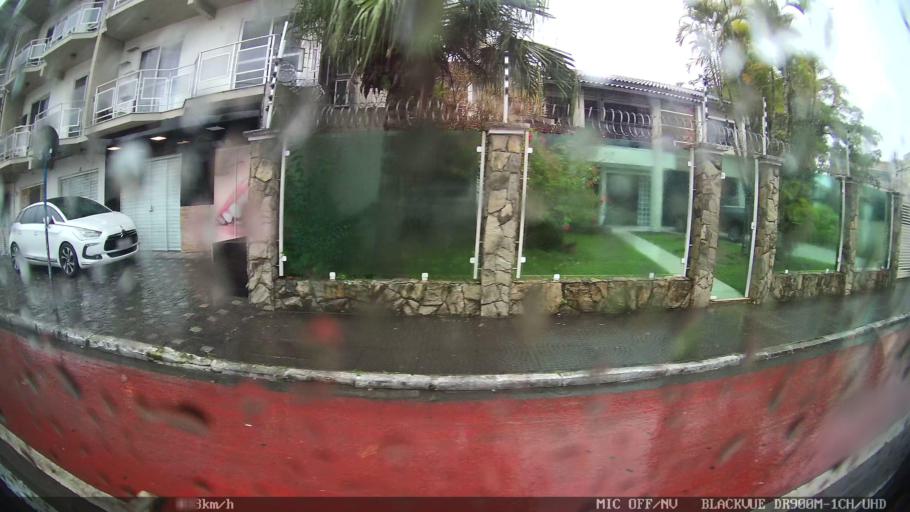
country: BR
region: Santa Catarina
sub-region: Itajai
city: Itajai
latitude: -26.9066
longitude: -48.6646
